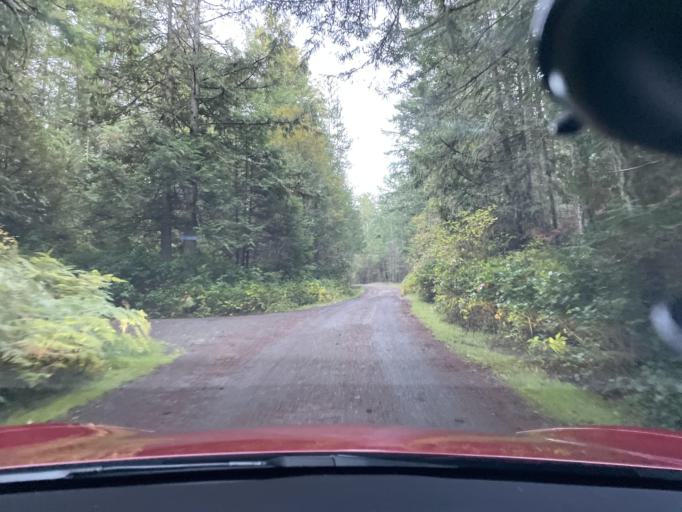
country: US
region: Washington
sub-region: San Juan County
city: Friday Harbor
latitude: 48.6176
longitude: -123.1407
